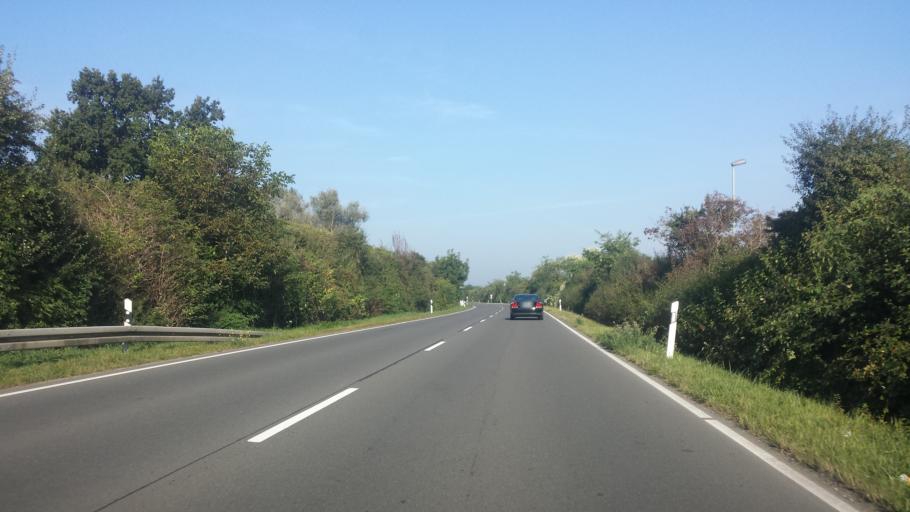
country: DE
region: Hesse
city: Lampertheim
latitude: 49.6091
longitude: 8.4493
